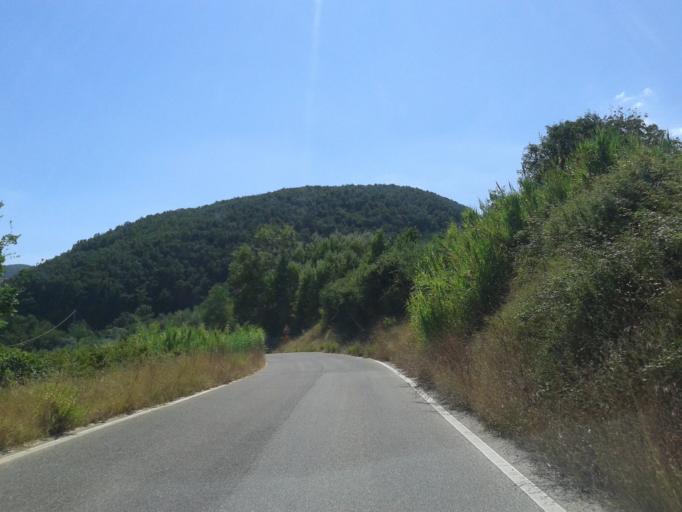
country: IT
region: Tuscany
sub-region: Province of Pisa
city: Chianni
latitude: 43.4708
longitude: 10.6334
